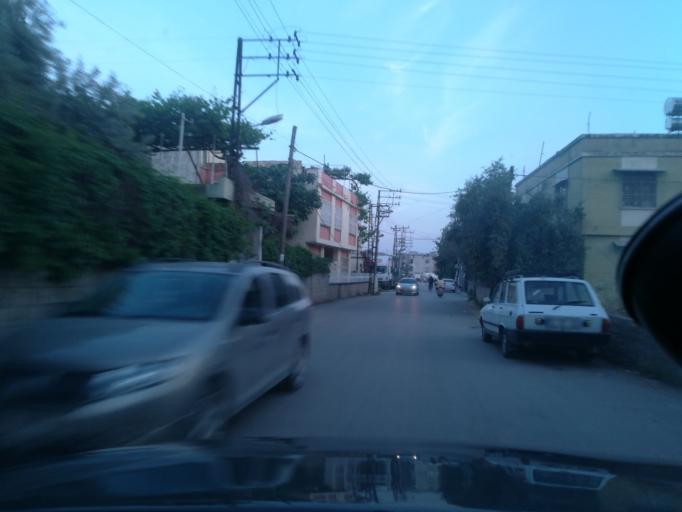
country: TR
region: Adana
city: Seyhan
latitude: 37.0169
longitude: 35.2799
